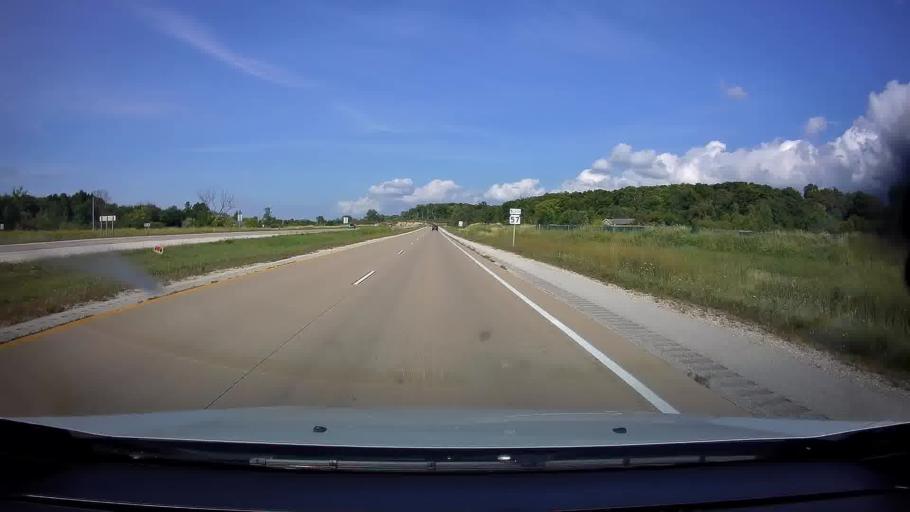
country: US
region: Wisconsin
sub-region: Kewaunee County
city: Luxemburg
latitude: 44.6780
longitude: -87.7288
